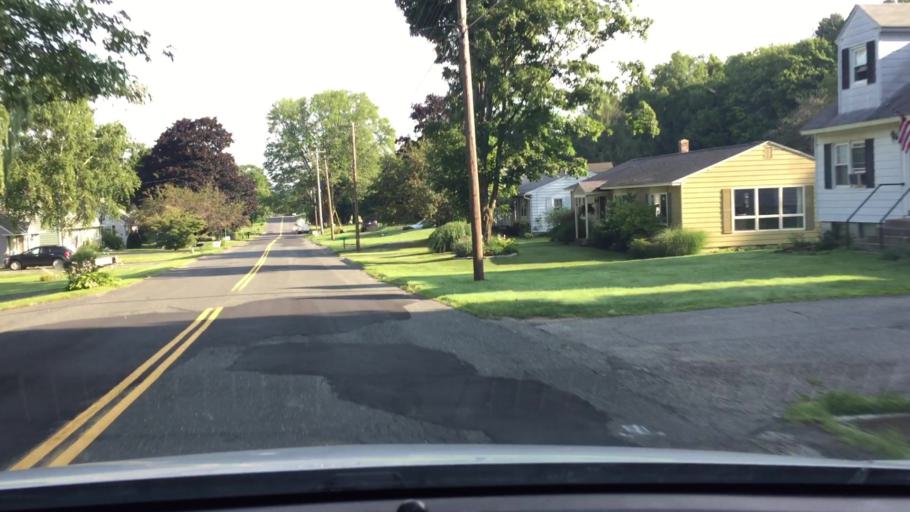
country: US
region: Massachusetts
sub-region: Berkshire County
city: Lee
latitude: 42.3090
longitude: -73.2315
